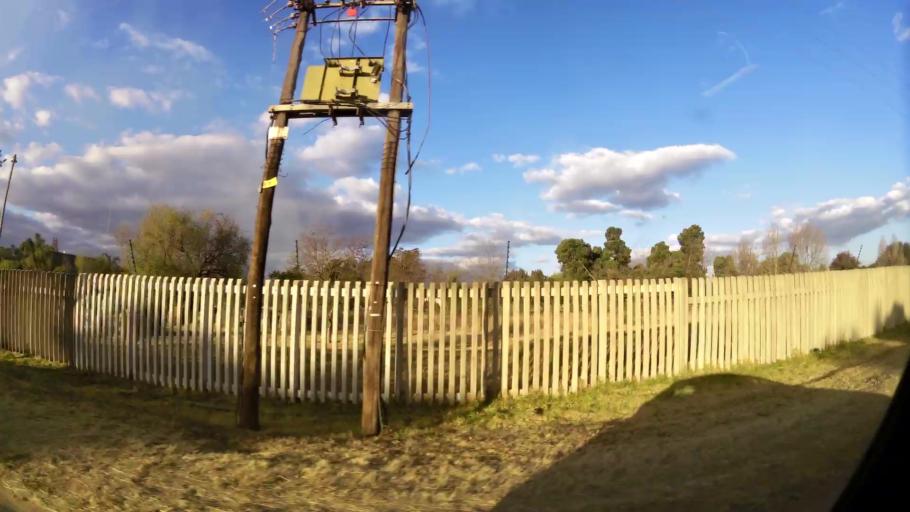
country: ZA
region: Gauteng
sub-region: City of Johannesburg Metropolitan Municipality
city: Midrand
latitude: -25.9500
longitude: 28.1543
